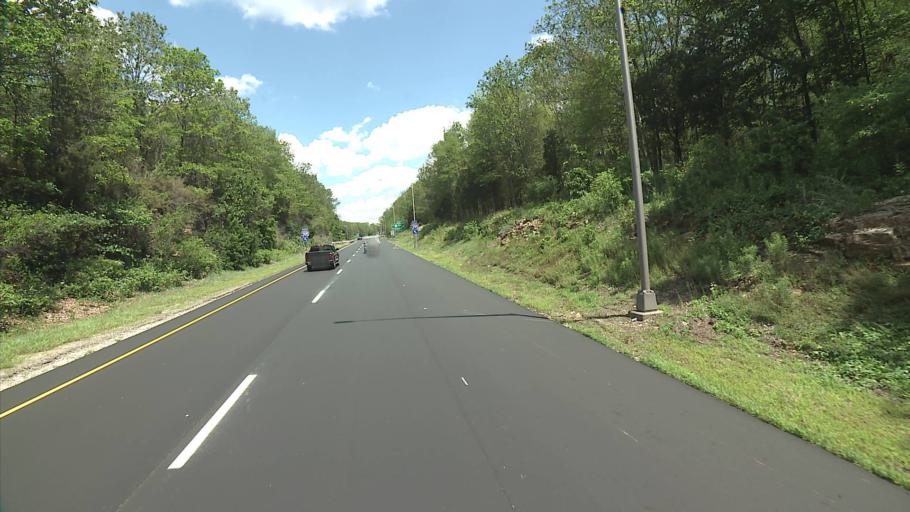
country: US
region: Connecticut
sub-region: Windham County
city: Wauregan
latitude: 41.7615
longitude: -71.8731
